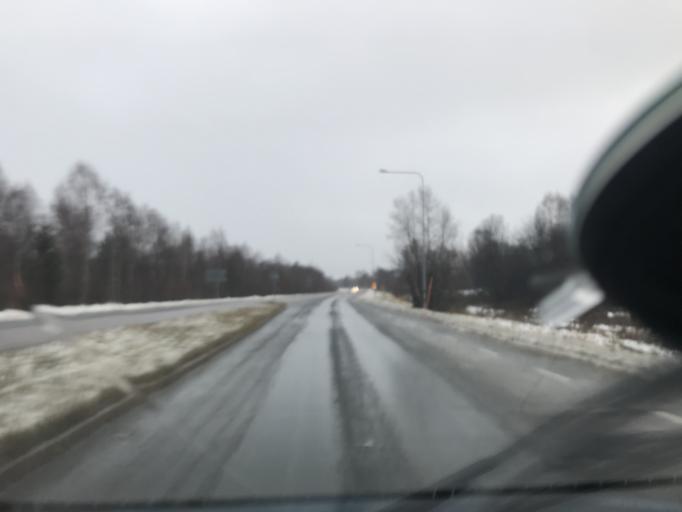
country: SE
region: Norrbotten
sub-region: Lulea Kommun
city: Sodra Sunderbyn
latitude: 65.6597
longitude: 21.9545
